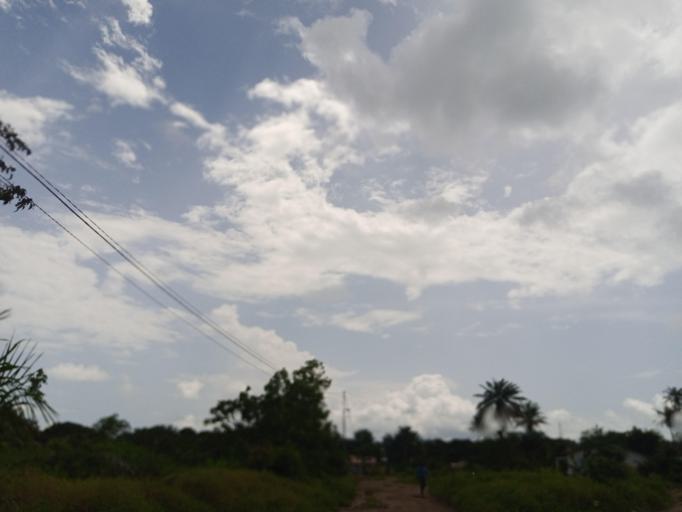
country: SL
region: Northern Province
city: Sawkta
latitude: 8.6333
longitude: -13.2049
